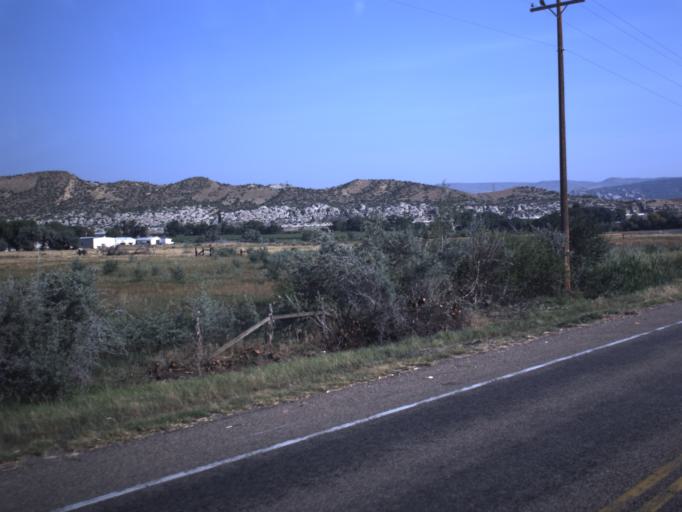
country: US
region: Utah
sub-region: Uintah County
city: Vernal
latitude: 40.4942
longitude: -109.5292
